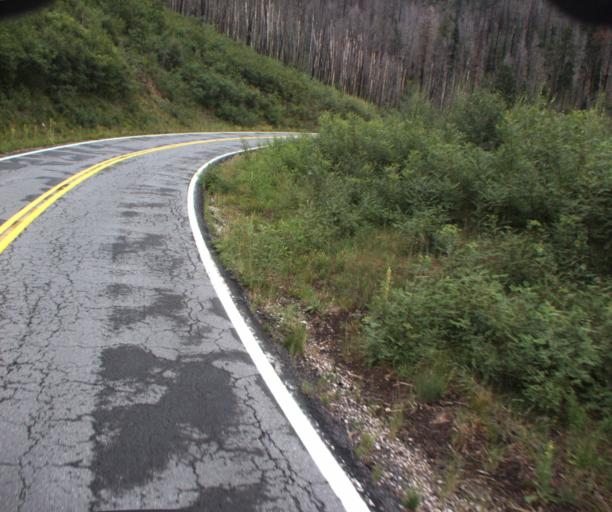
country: US
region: Arizona
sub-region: Apache County
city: Eagar
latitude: 33.8147
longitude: -109.1617
